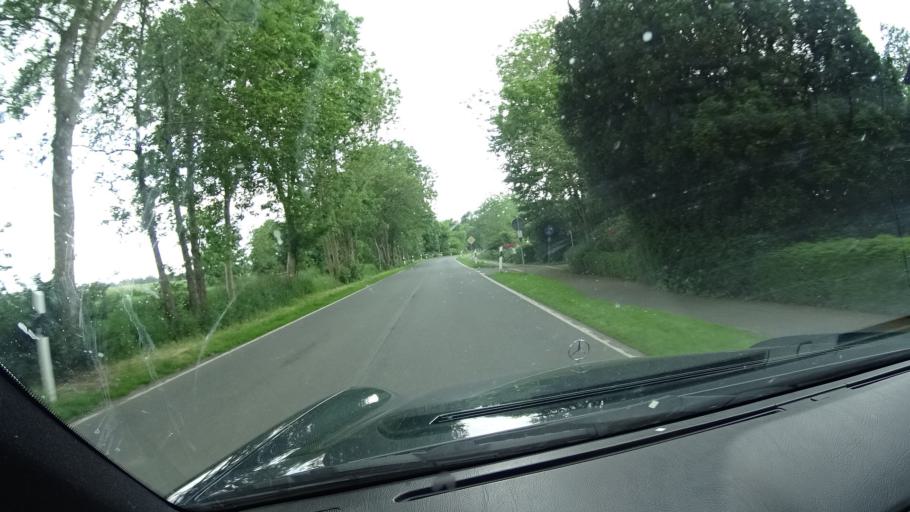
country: DE
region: Lower Saxony
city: Butjadingen
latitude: 53.5779
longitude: 8.2666
